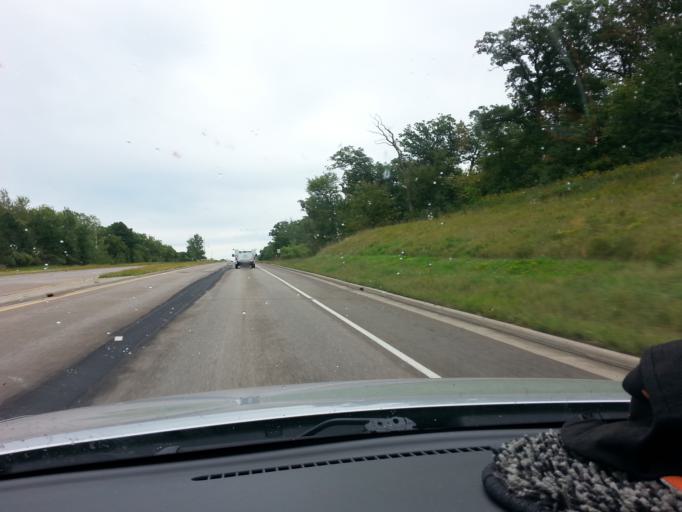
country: US
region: Minnesota
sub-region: Scott County
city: Prior Lake
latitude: 44.6814
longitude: -93.3450
